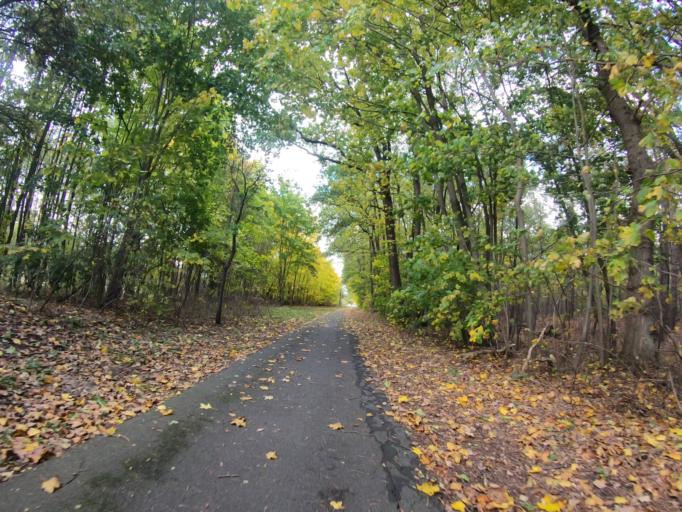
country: DE
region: Lower Saxony
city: Wagenhoff
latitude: 52.5501
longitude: 10.5145
